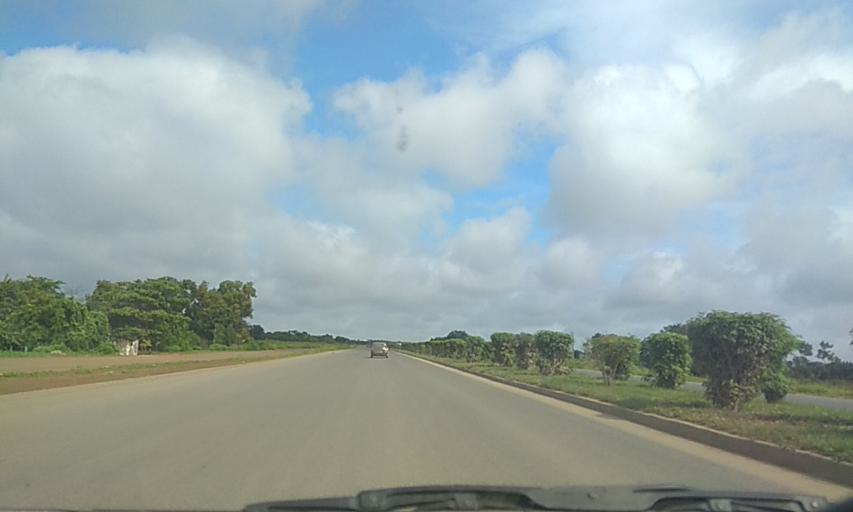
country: IN
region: Karnataka
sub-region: Haveri
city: Shiggaon
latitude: 14.9976
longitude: 75.2098
